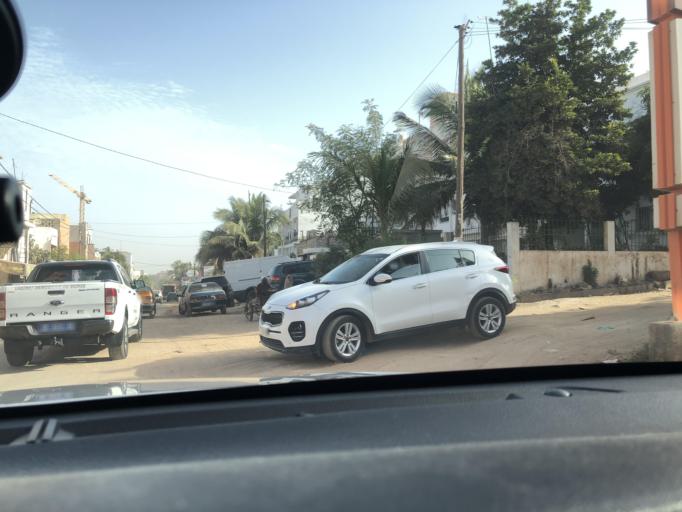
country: SN
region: Dakar
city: Mermoz Boabab
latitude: 14.7279
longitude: -17.5003
